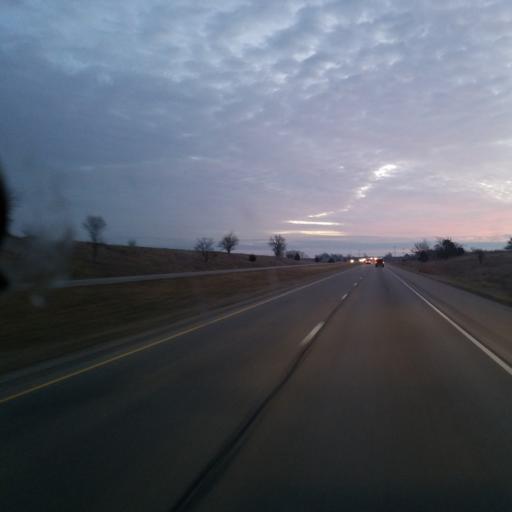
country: US
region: Illinois
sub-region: Tazewell County
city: Morton
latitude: 40.6214
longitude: -89.4175
